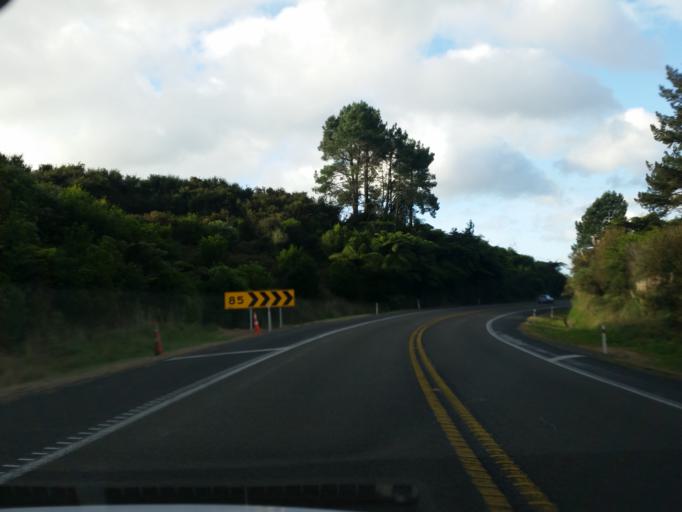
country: NZ
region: Bay of Plenty
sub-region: Western Bay of Plenty District
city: Katikati
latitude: -37.6460
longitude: 175.9844
